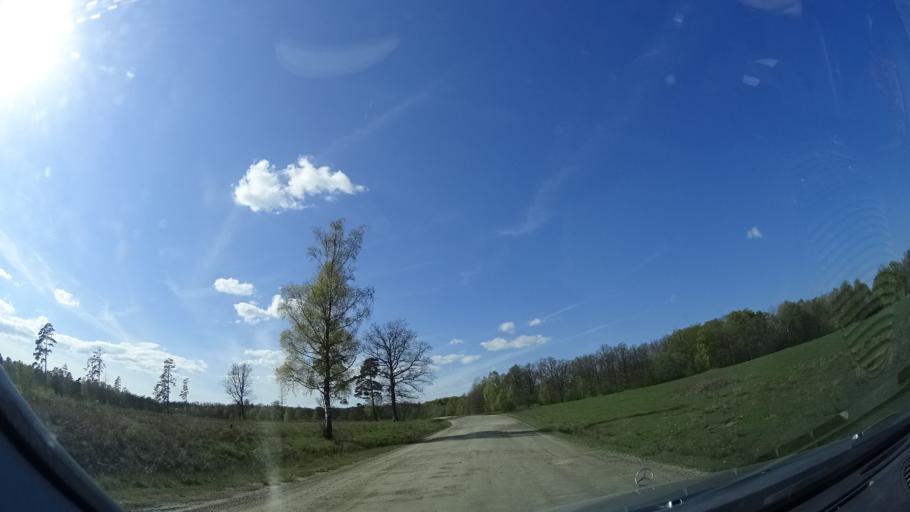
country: SE
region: Skane
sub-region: Hassleholms Kommun
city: Tormestorp
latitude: 56.1105
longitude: 13.6951
